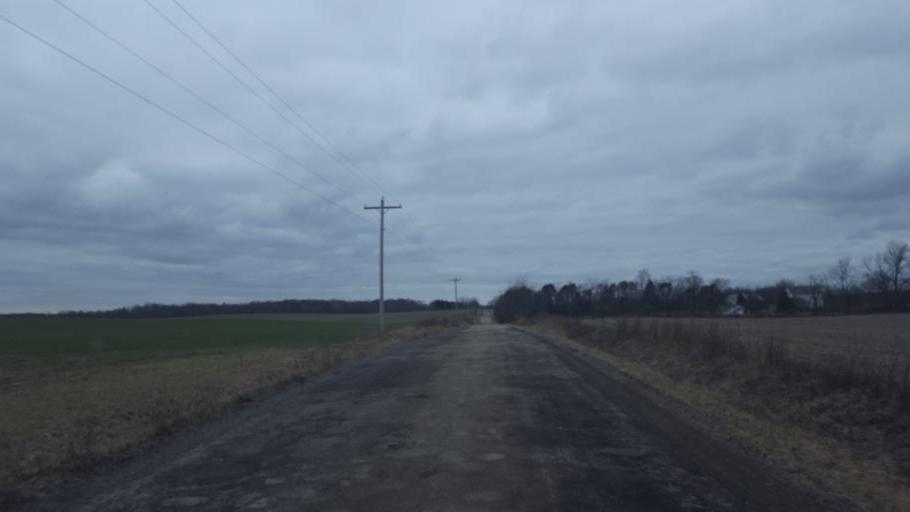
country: US
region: Ohio
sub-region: Morrow County
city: Mount Gilead
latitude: 40.5736
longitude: -82.7644
